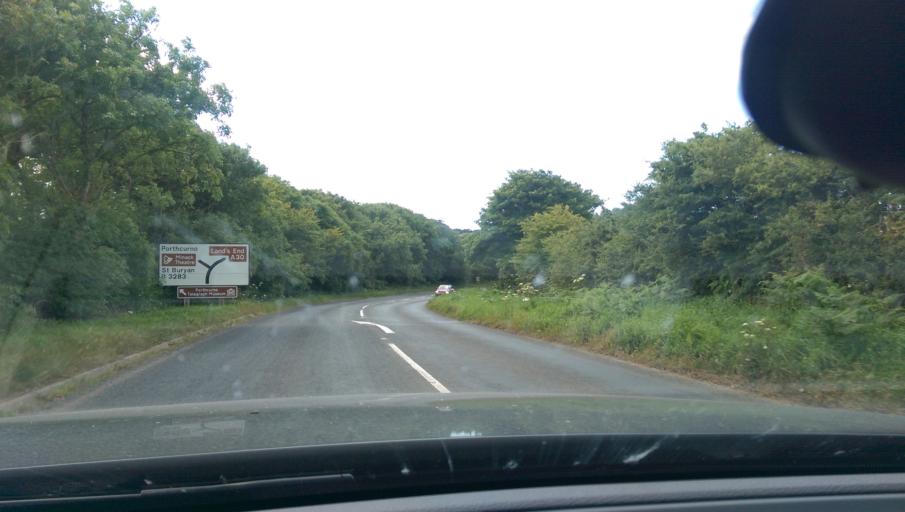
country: GB
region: England
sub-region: Cornwall
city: St. Buryan
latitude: 50.0970
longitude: -5.5926
